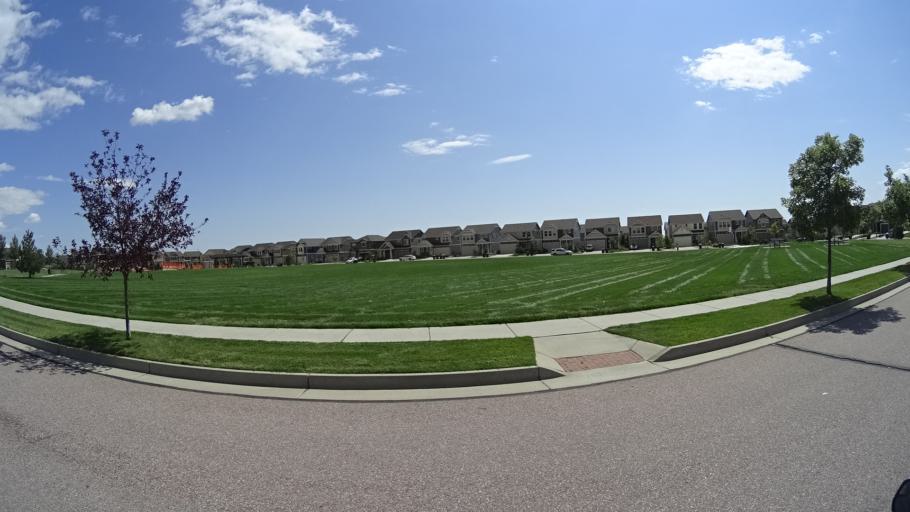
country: US
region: Colorado
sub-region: El Paso County
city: Cimarron Hills
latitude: 38.9289
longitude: -104.6733
